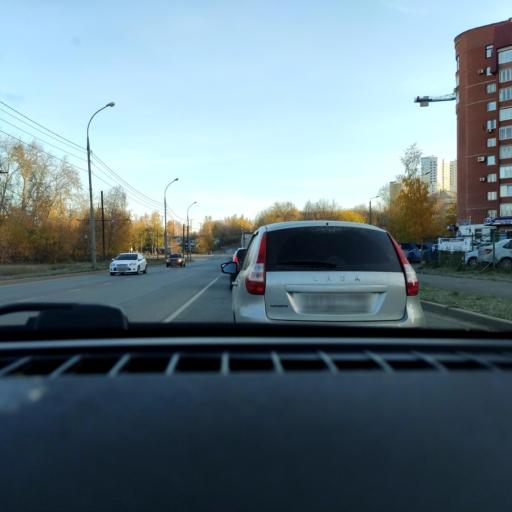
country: RU
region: Perm
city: Perm
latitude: 58.0071
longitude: 56.1934
